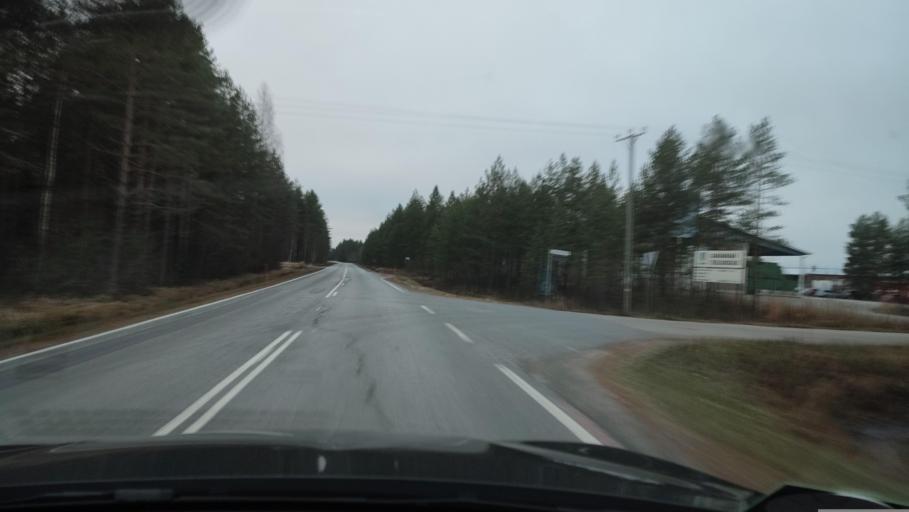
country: FI
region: Southern Ostrobothnia
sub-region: Suupohja
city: Karijoki
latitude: 62.3236
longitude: 21.7734
